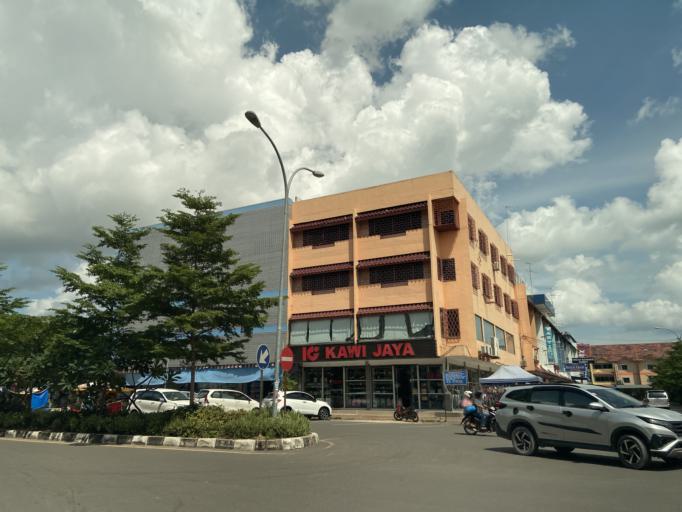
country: SG
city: Singapore
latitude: 1.1477
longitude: 104.0083
